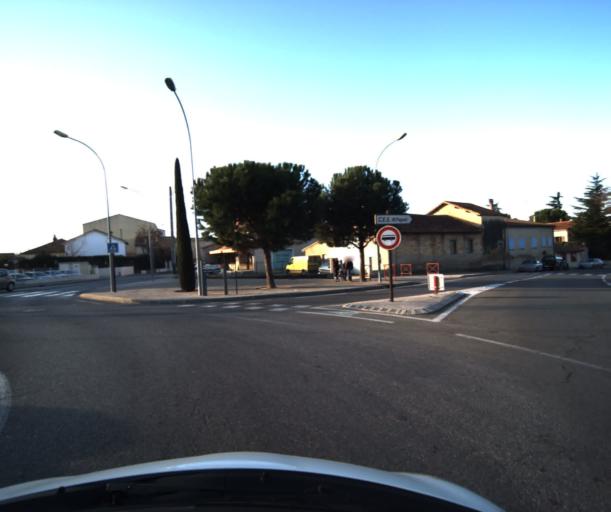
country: FR
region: Provence-Alpes-Cote d'Azur
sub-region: Departement du Vaucluse
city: Pertuis
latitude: 43.6939
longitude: 5.5090
